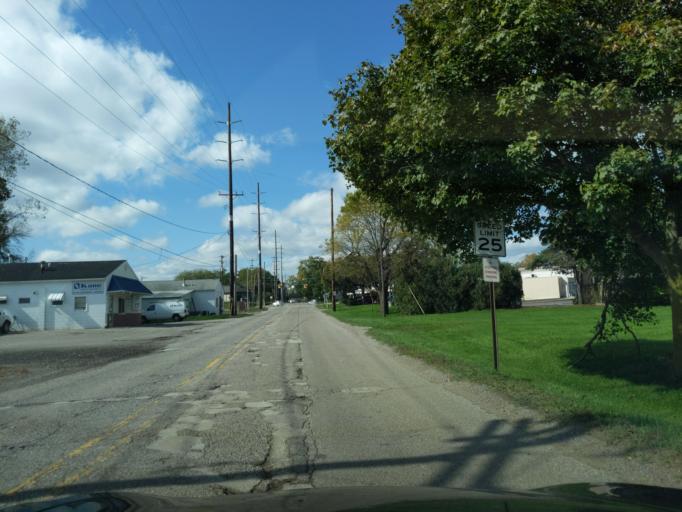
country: US
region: Michigan
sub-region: Eaton County
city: Charlotte
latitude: 42.5677
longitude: -84.8259
